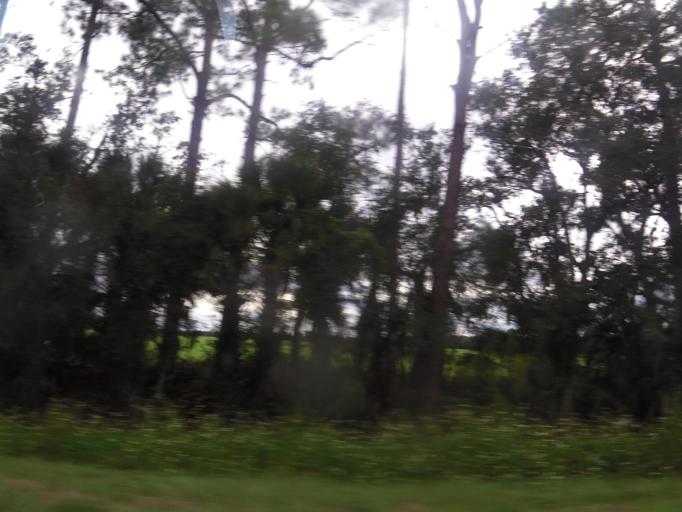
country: US
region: Florida
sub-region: Flagler County
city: Bunnell
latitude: 29.4954
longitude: -81.3476
